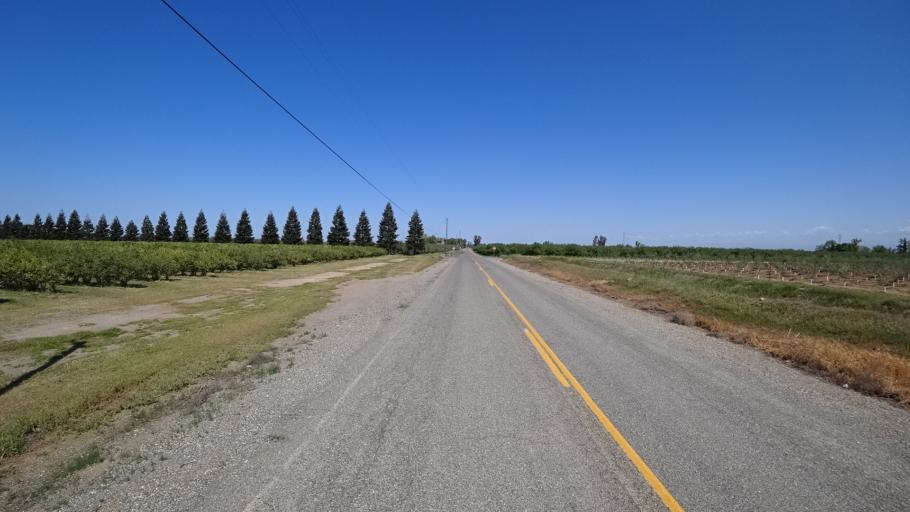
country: US
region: California
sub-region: Glenn County
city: Orland
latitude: 39.7862
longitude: -122.1690
